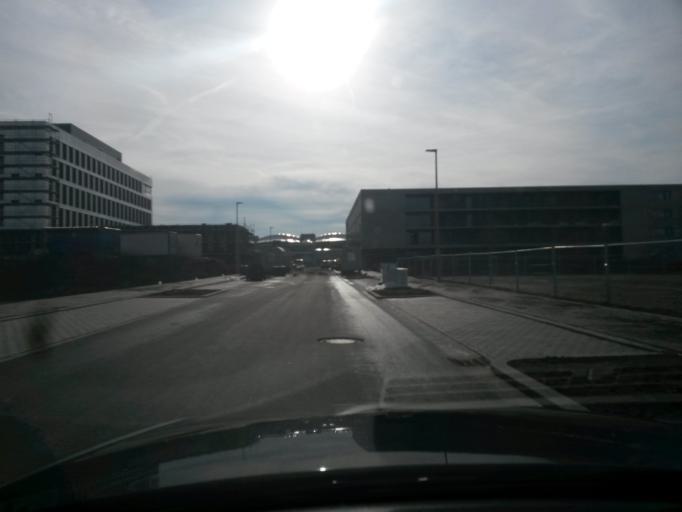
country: DE
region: Bavaria
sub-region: Regierungsbezirk Unterfranken
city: Wuerzburg
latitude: 49.7881
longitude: 9.9674
